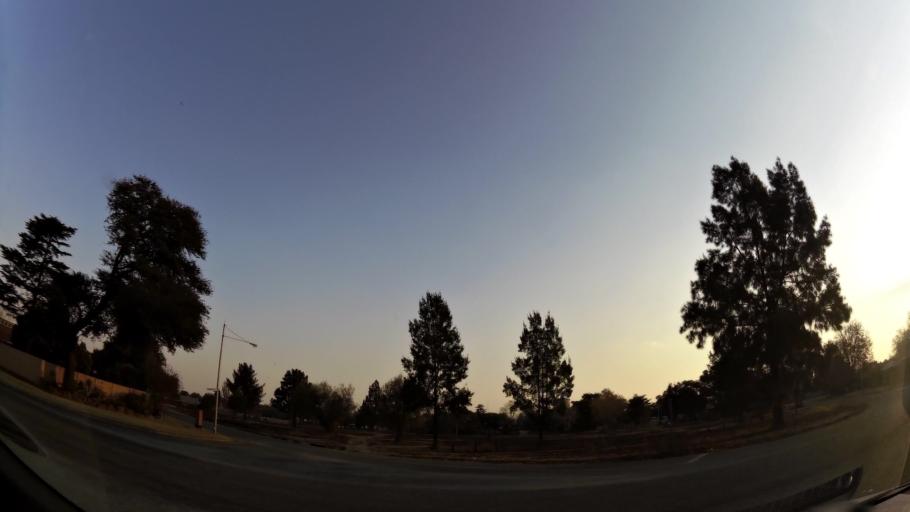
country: ZA
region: Gauteng
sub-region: Ekurhuleni Metropolitan Municipality
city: Springs
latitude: -26.3052
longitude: 28.4515
